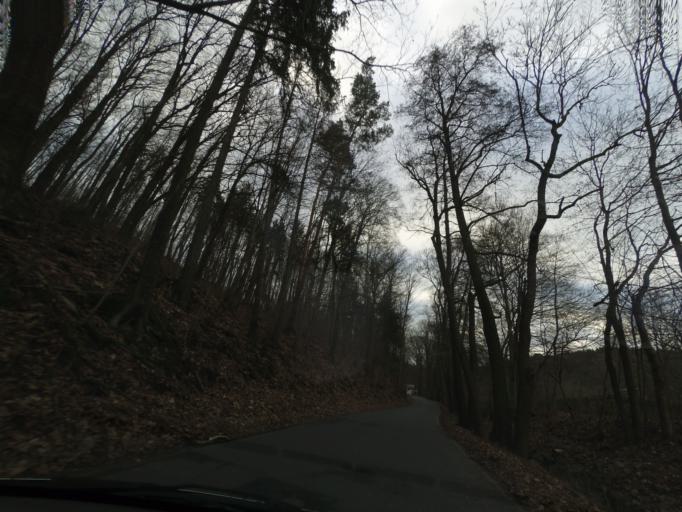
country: DE
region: Thuringia
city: Saalfeld
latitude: 50.6372
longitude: 11.3452
